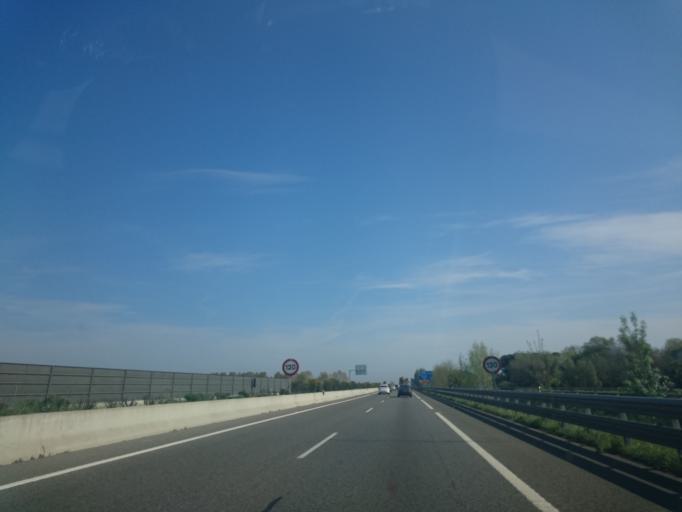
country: ES
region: Catalonia
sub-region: Provincia de Girona
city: Vilobi d'Onyar
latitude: 41.8741
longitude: 2.7791
